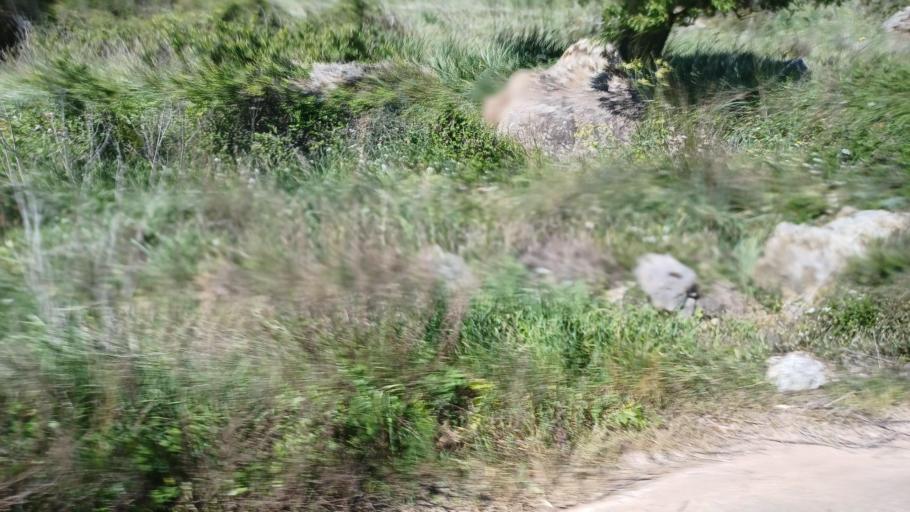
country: CY
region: Pafos
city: Polis
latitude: 34.9697
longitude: 32.3965
